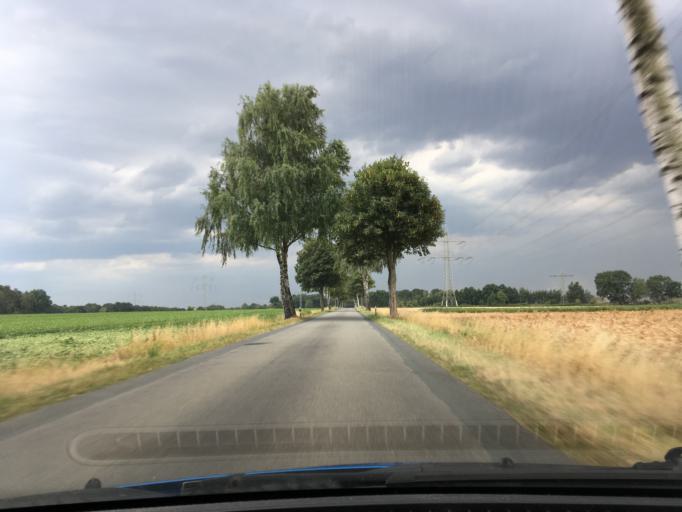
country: DE
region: Lower Saxony
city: Hanstedt Eins
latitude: 53.0761
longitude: 10.3845
